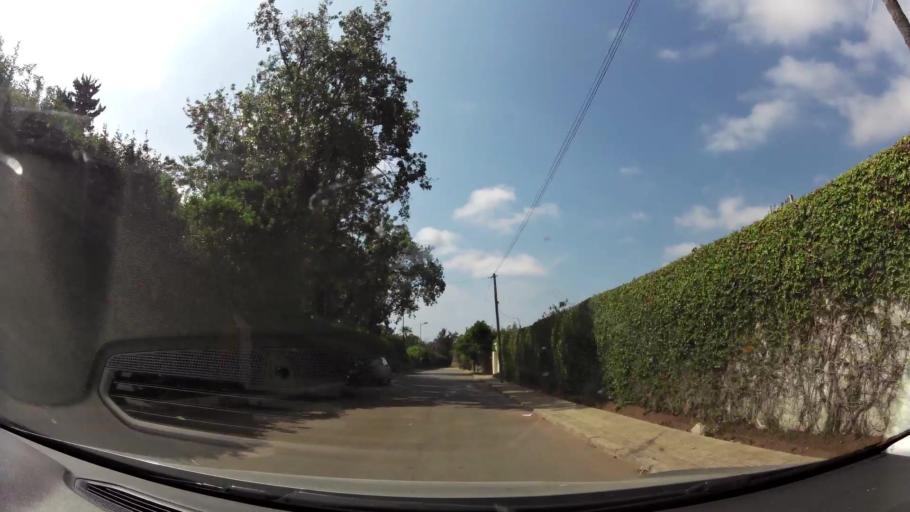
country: MA
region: Rabat-Sale-Zemmour-Zaer
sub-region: Rabat
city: Rabat
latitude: 33.9842
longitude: -6.8379
